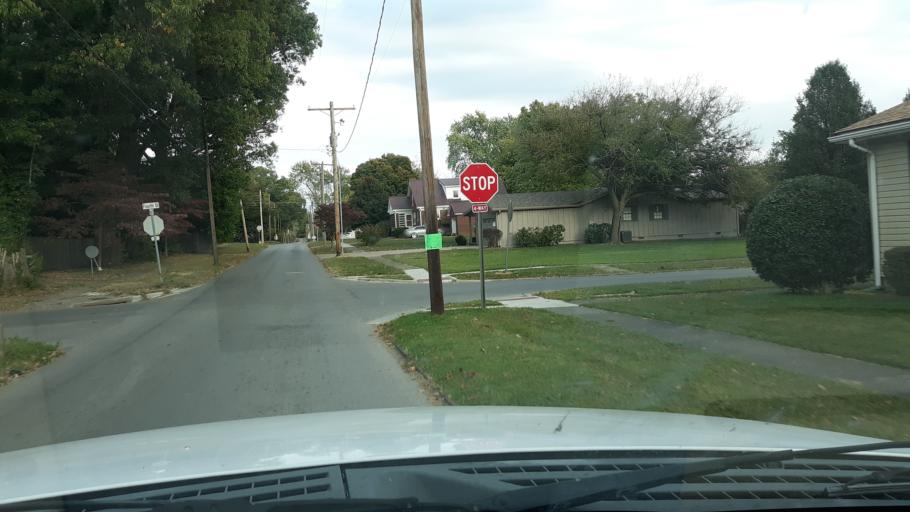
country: US
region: Illinois
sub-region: Saline County
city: Eldorado
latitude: 37.8161
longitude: -88.4398
